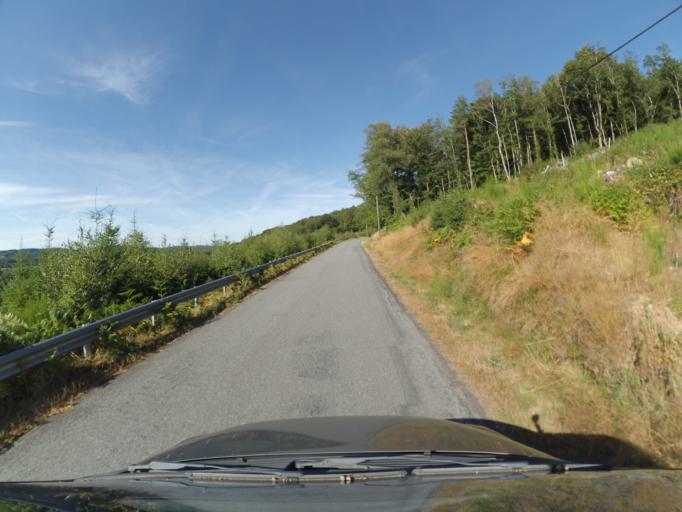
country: FR
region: Limousin
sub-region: Departement de la Correze
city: Bugeat
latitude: 45.6891
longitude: 1.9706
